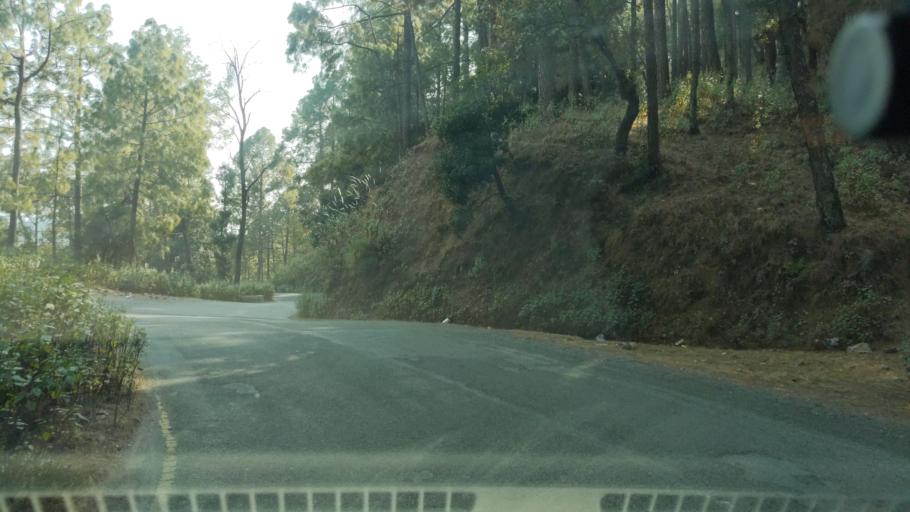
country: IN
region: Uttarakhand
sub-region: Naini Tal
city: Bhowali
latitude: 29.3939
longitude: 79.5392
